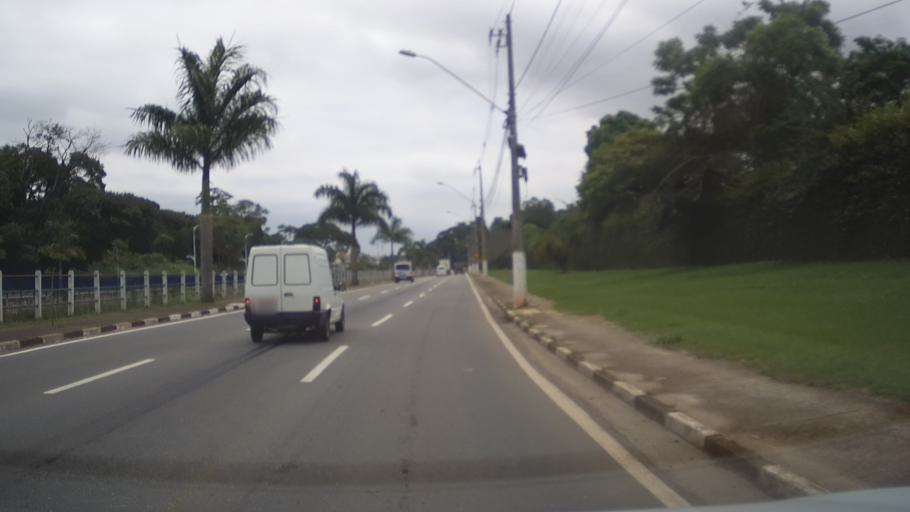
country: BR
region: Sao Paulo
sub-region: Aruja
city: Aruja
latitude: -23.4107
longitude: -46.3672
